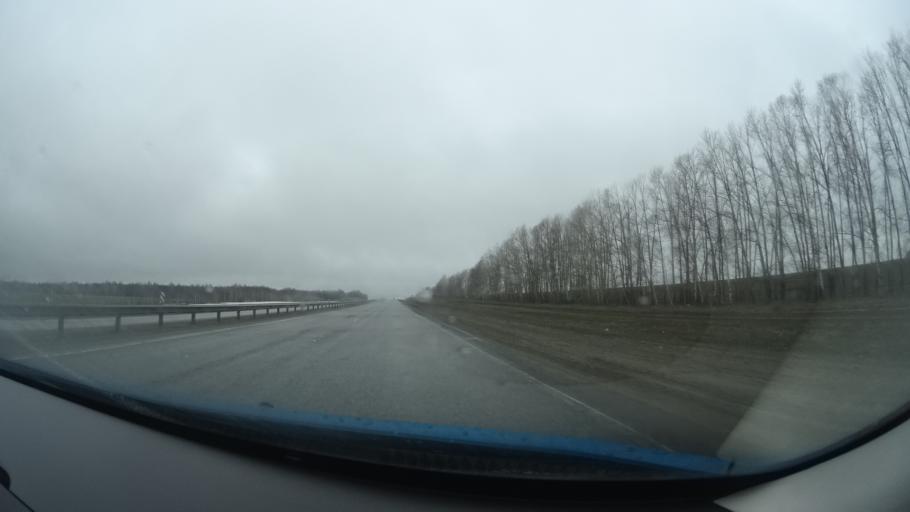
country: RU
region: Bashkortostan
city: Alekseyevka
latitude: 54.7324
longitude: 55.1329
